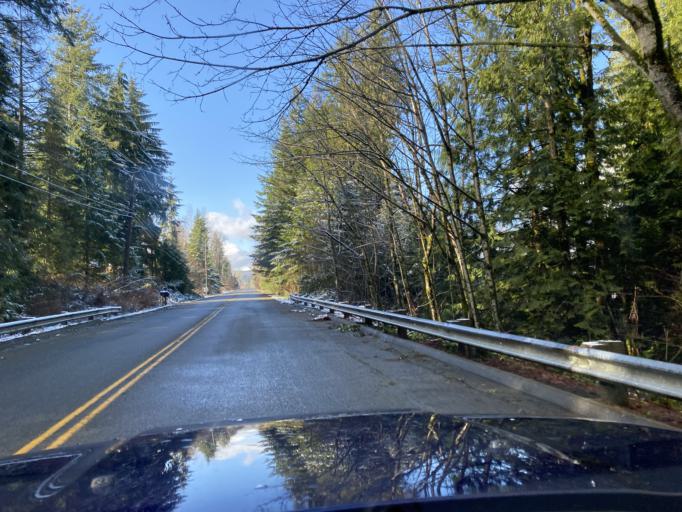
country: US
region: Washington
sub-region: King County
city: Snoqualmie
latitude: 47.5145
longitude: -121.8674
